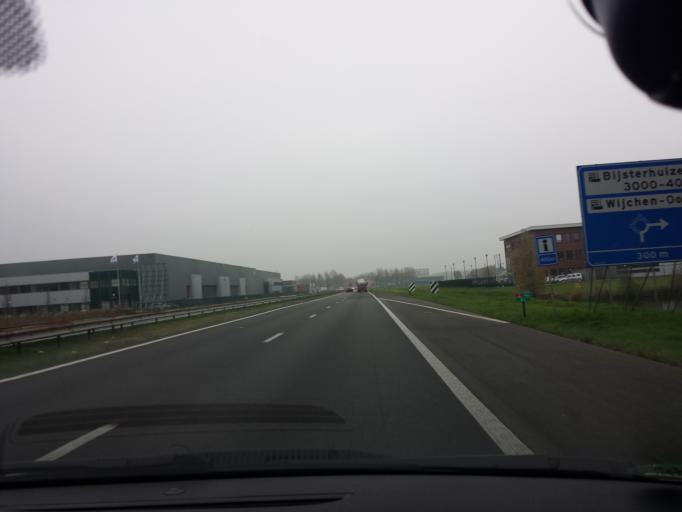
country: NL
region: Gelderland
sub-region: Gemeente Wijchen
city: Wijchen
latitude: 51.8260
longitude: 5.7479
